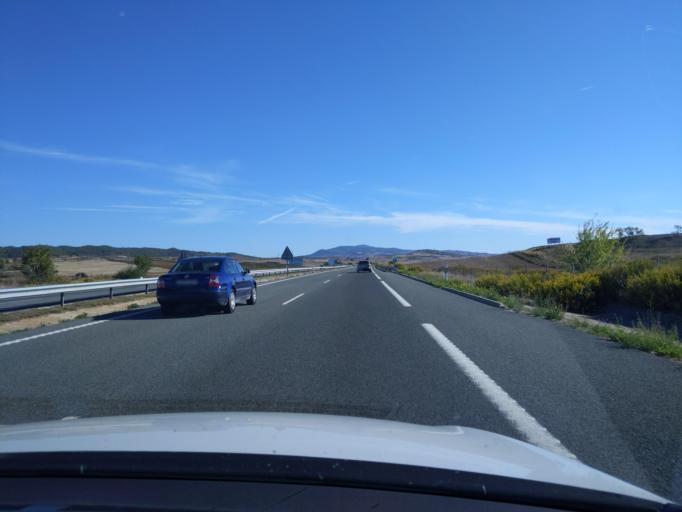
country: ES
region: Navarre
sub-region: Provincia de Navarra
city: Los Arcos
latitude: 42.5651
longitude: -2.1725
